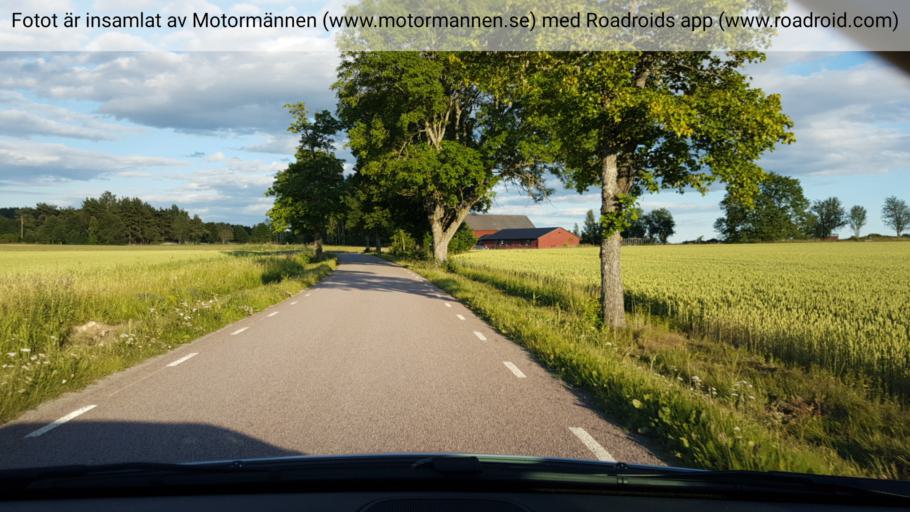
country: SE
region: Vaestmanland
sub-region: Vasteras
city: Tillberga
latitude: 59.6838
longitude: 16.6936
